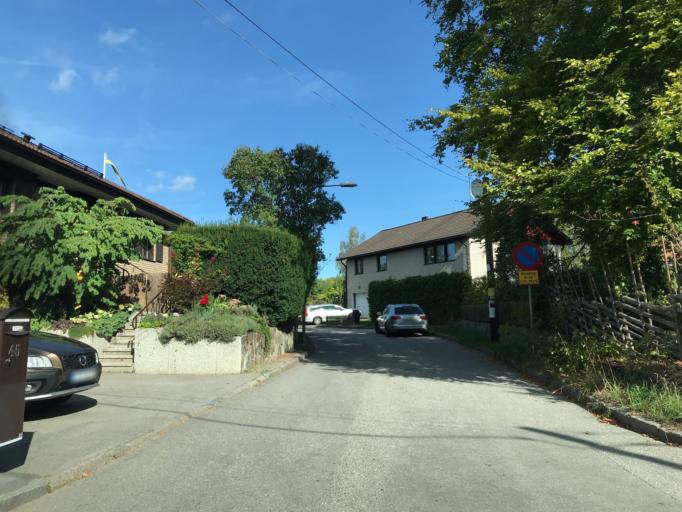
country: SE
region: Stockholm
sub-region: Huddinge Kommun
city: Segeltorp
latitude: 59.2751
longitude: 17.9562
